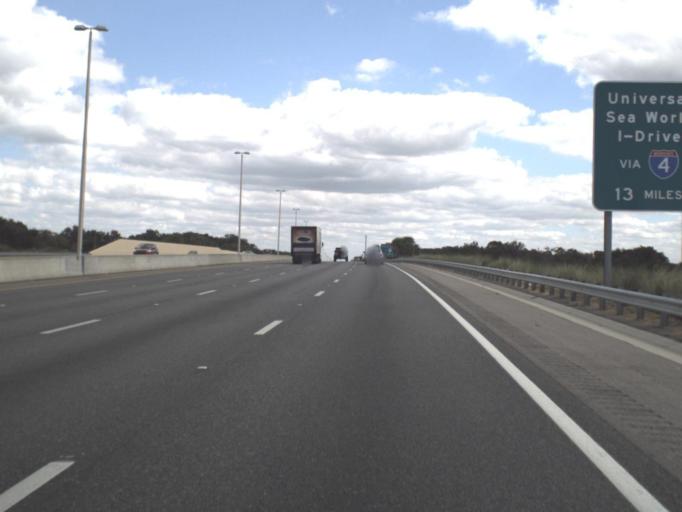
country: US
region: Florida
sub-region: Orange County
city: Oakland
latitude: 28.5450
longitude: -81.6112
